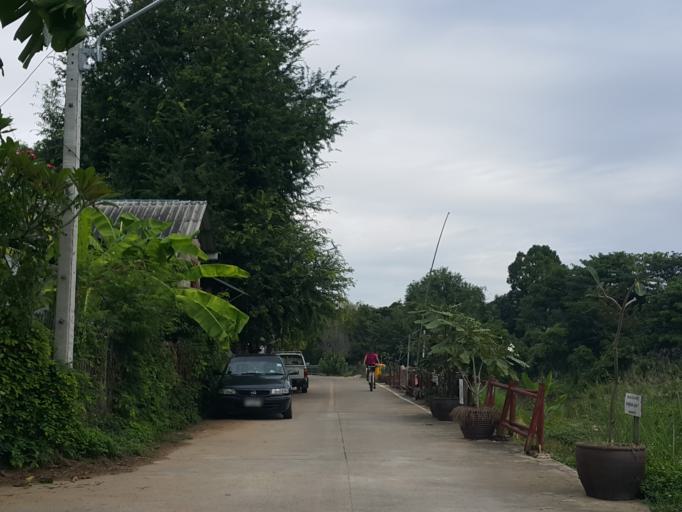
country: TH
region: Lampang
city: Lampang
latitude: 18.2950
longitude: 99.5124
